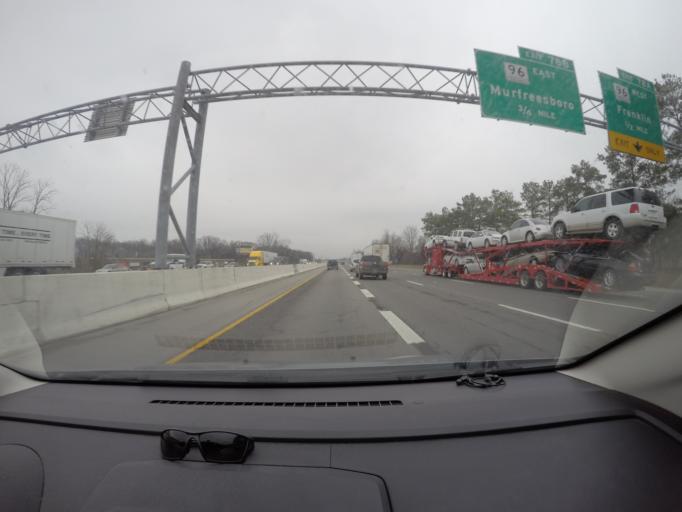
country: US
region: Tennessee
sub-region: Rutherford County
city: Murfreesboro
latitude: 35.8561
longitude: -86.4451
